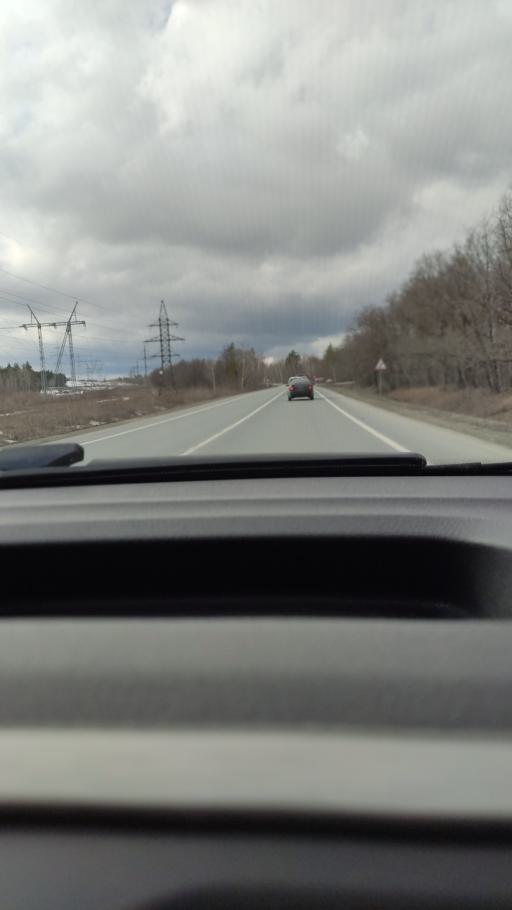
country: RU
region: Samara
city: Pribrezhnyy
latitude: 53.5085
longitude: 49.9337
